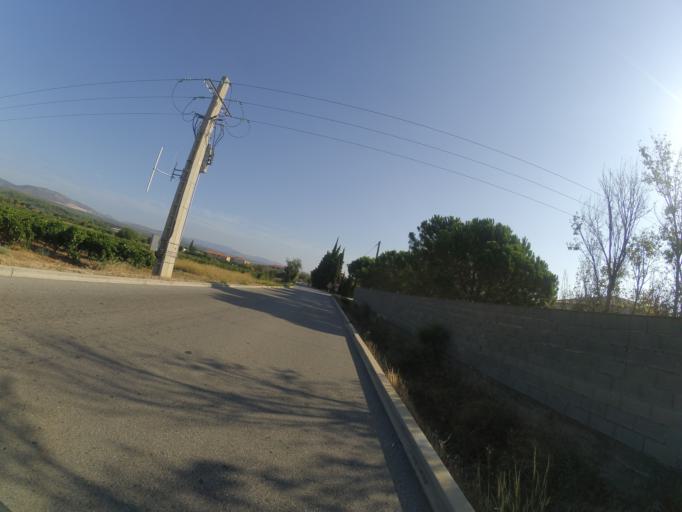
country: FR
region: Languedoc-Roussillon
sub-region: Departement des Pyrenees-Orientales
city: Peyrestortes
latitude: 42.7712
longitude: 2.8303
